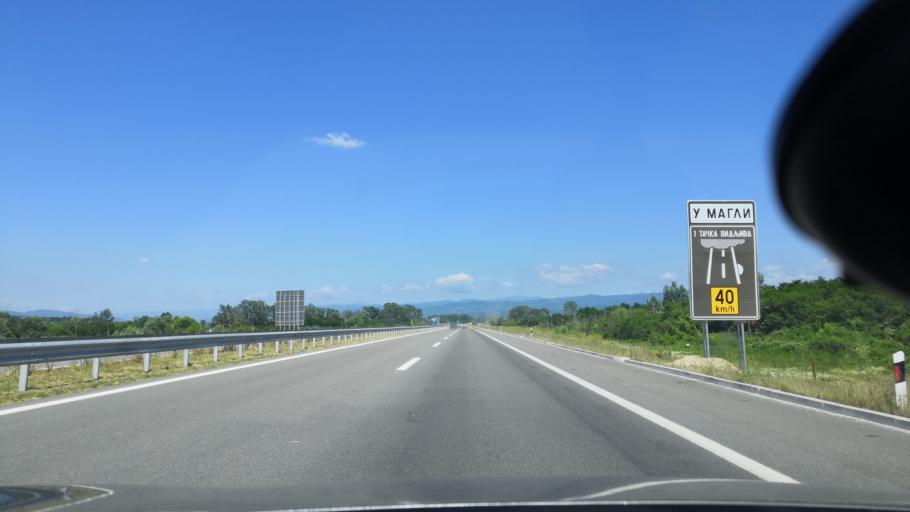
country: RS
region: Central Serbia
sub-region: Pcinjski Okrug
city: Bujanovac
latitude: 42.4520
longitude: 21.7883
